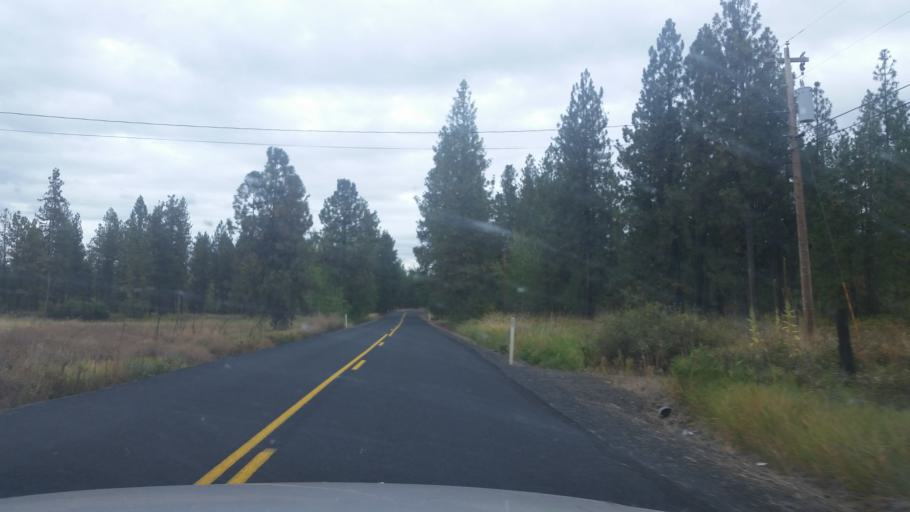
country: US
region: Washington
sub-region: Spokane County
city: Medical Lake
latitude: 47.4978
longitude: -117.7714
